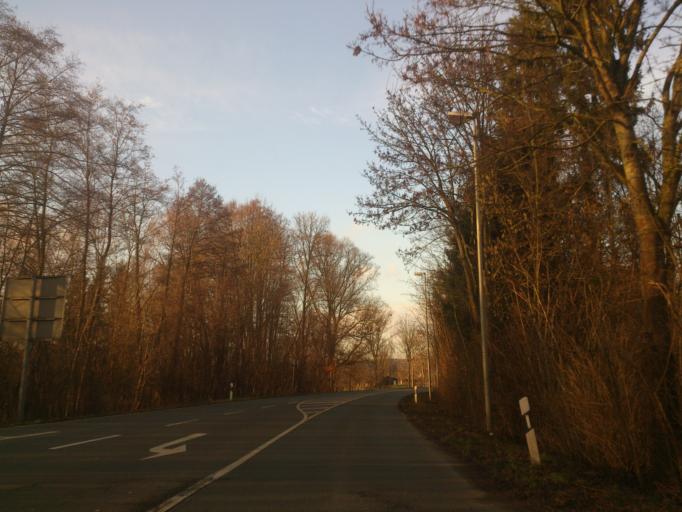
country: DE
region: North Rhine-Westphalia
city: Brakel
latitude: 51.7197
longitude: 9.1869
